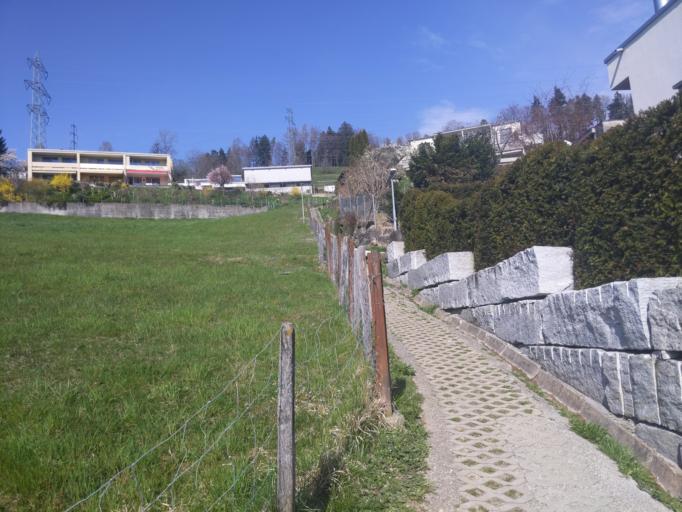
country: CH
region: Saint Gallen
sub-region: Wahlkreis See-Gaster
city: Schmerikon
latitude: 47.2277
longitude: 8.9461
